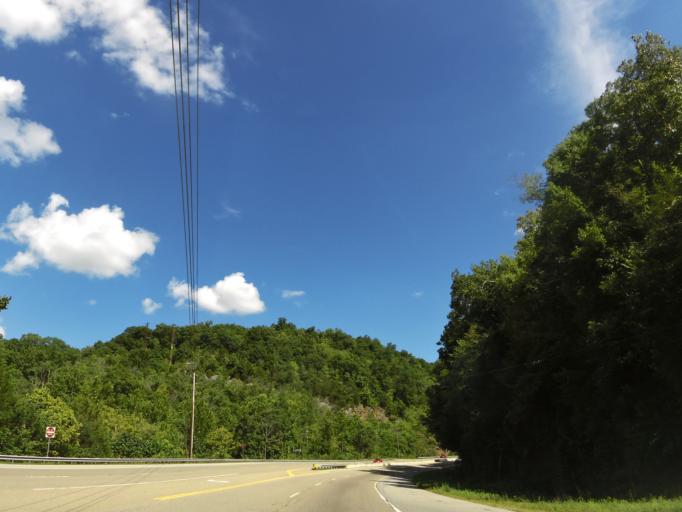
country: US
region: Tennessee
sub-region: Grainger County
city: Rutledge
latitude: 36.3762
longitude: -83.4432
